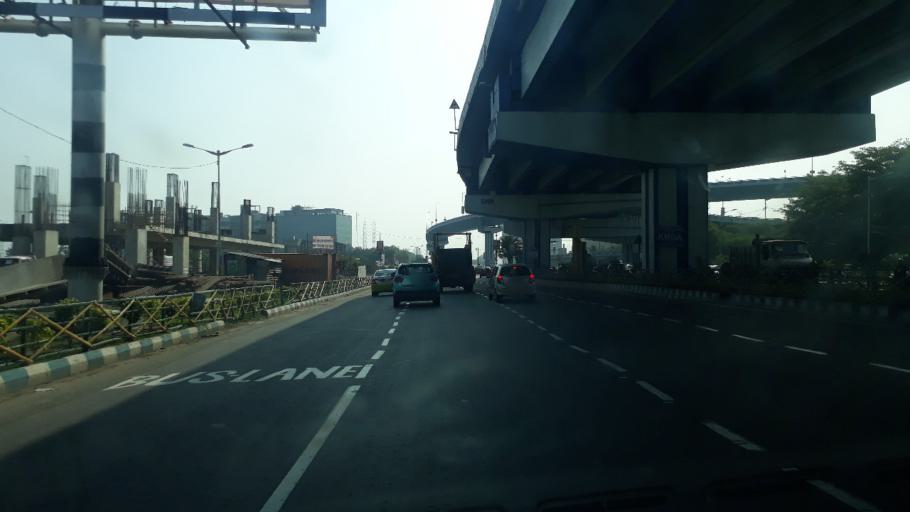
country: IN
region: West Bengal
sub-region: Kolkata
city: Kolkata
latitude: 22.5443
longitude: 88.3990
